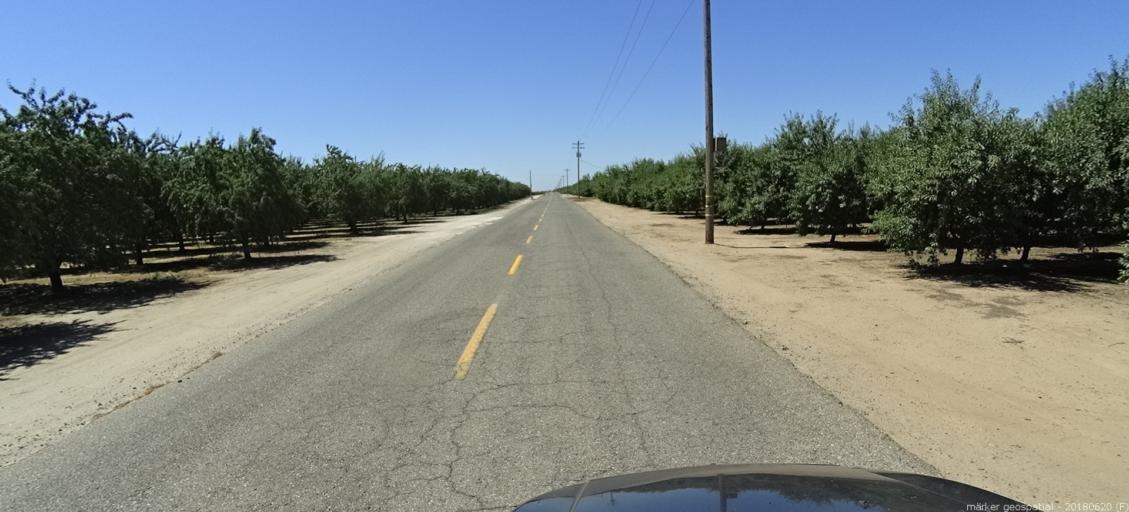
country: US
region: California
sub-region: Madera County
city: Parkwood
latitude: 36.8867
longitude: -120.0015
